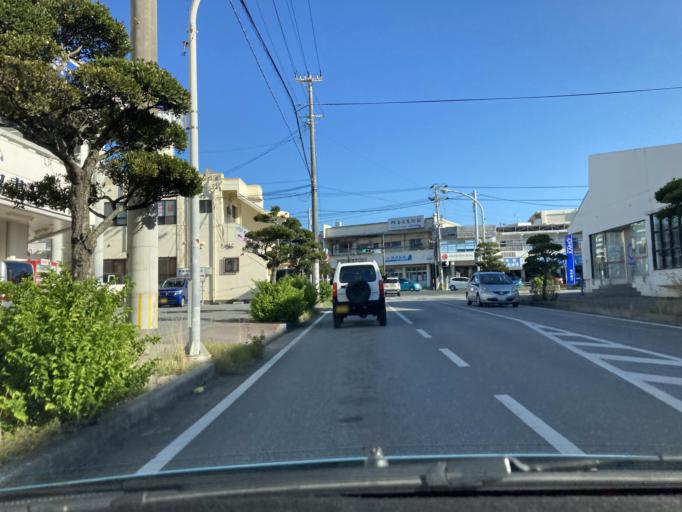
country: JP
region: Okinawa
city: Ginowan
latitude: 26.2779
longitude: 127.7777
